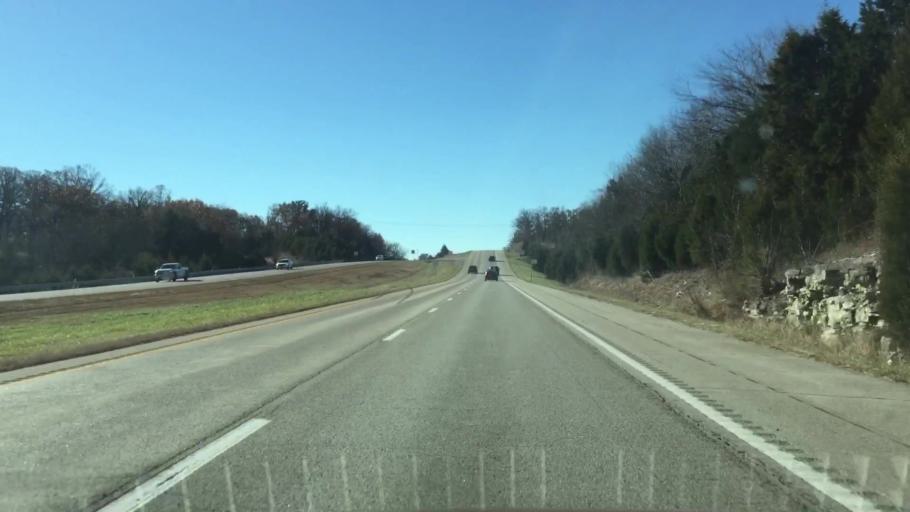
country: US
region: Missouri
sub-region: Cole County
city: Wardsville
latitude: 38.4628
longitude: -92.2950
